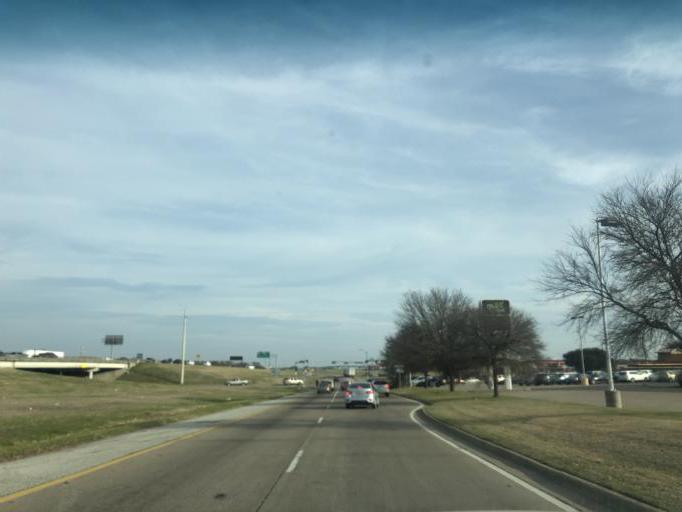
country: US
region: Texas
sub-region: Dallas County
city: Duncanville
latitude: 32.6598
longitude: -96.8929
